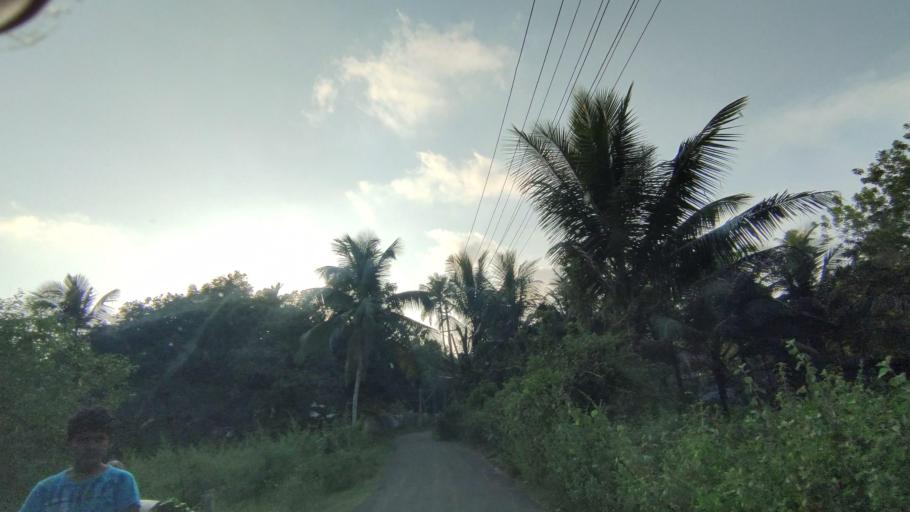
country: IN
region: Kerala
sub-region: Alappuzha
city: Shertallai
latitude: 9.6508
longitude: 76.3539
